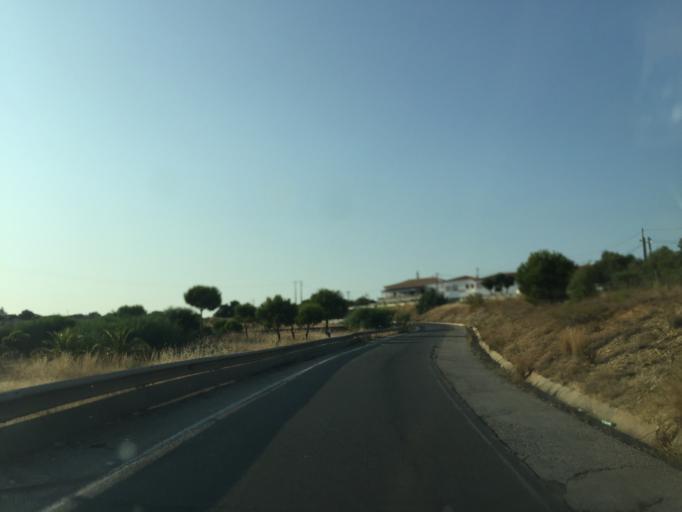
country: PT
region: Faro
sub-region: Loule
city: Almancil
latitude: 37.0827
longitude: -8.0117
